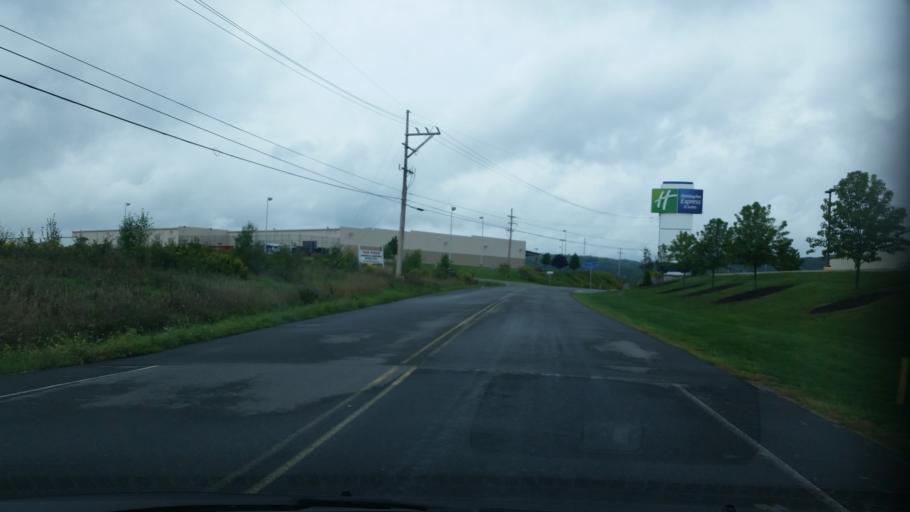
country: US
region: Pennsylvania
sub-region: Clearfield County
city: Clearfield
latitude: 41.0335
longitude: -78.3939
